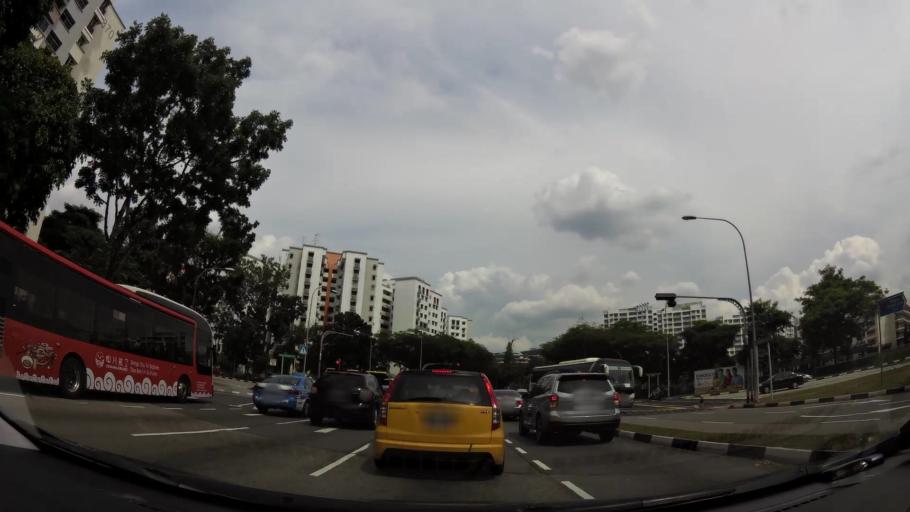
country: MY
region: Johor
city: Johor Bahru
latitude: 1.4322
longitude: 103.7874
